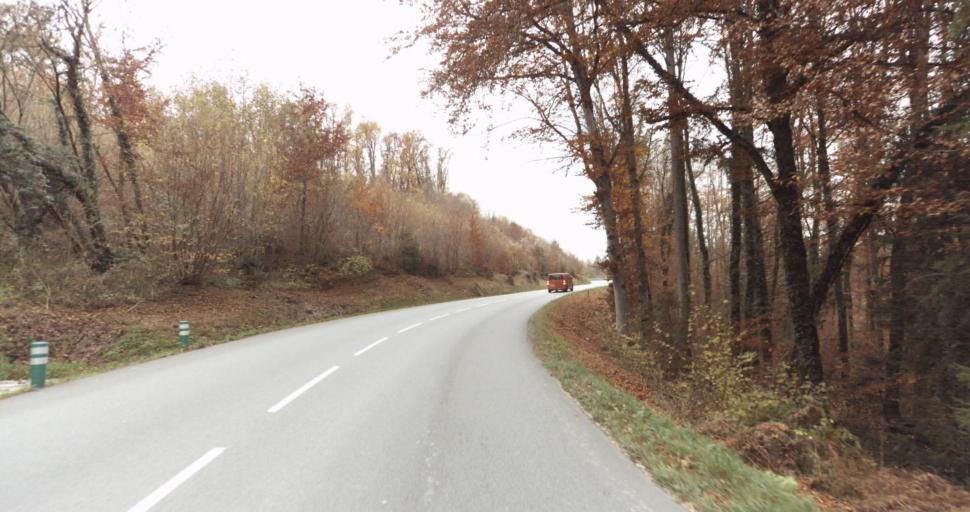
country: FR
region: Rhone-Alpes
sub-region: Departement de la Haute-Savoie
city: Chavanod
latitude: 45.8785
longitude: 6.0326
